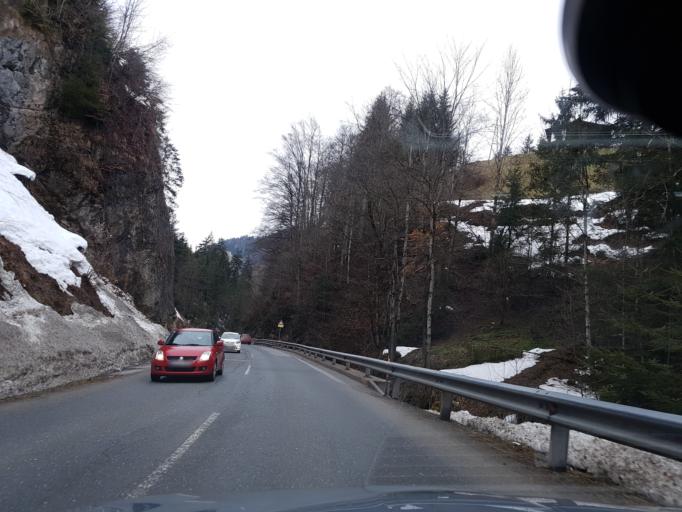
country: AT
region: Tyrol
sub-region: Politischer Bezirk Kufstein
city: Worgl
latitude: 47.4585
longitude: 12.0952
